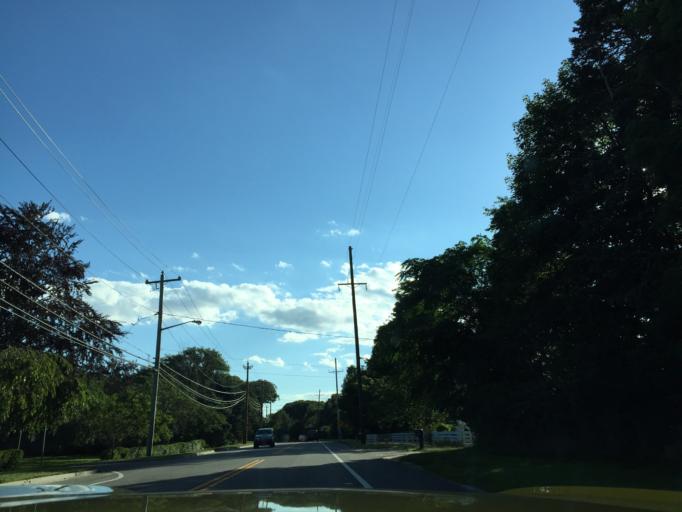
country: US
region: New York
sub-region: Suffolk County
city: Greenport West
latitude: 41.1132
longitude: -72.3701
